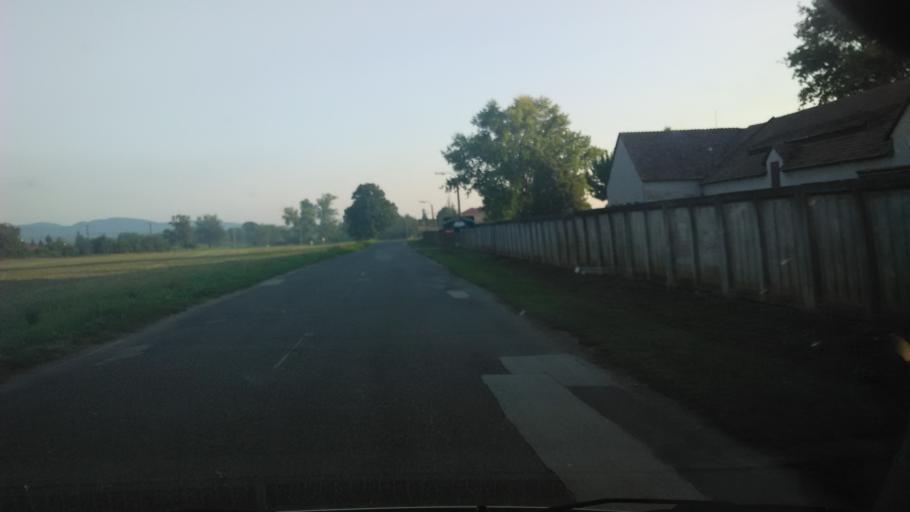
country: SK
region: Nitriansky
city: Zeliezovce
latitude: 48.0231
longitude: 18.8006
